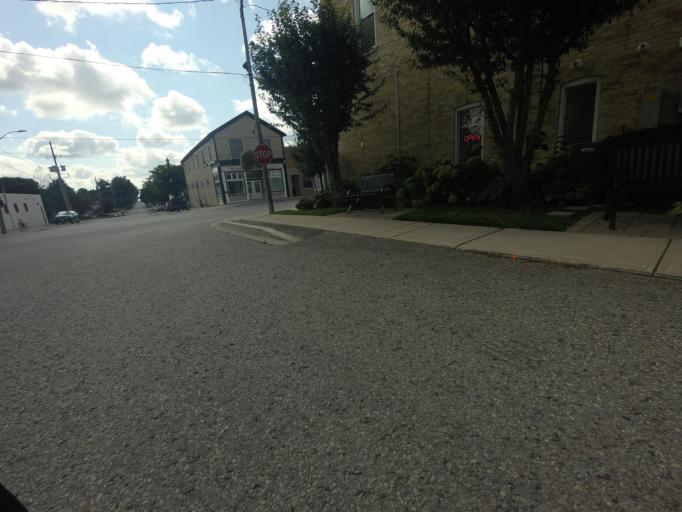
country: CA
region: Ontario
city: Huron East
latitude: 43.7365
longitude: -81.4296
